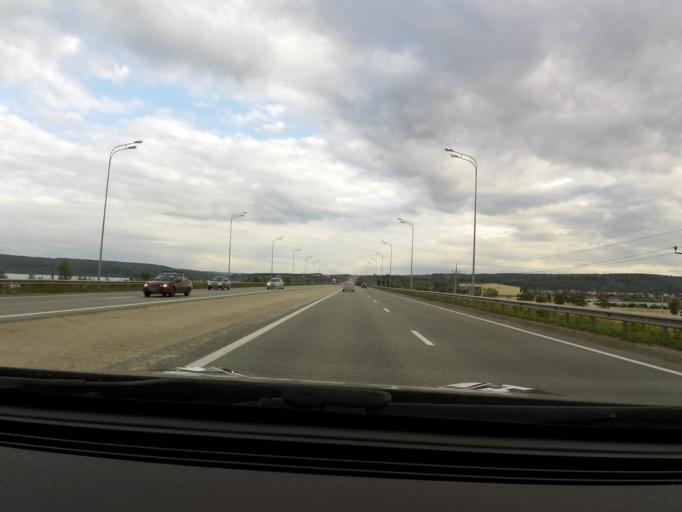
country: RU
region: Tatarstan
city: Osinovo
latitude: 55.8021
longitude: 48.8414
